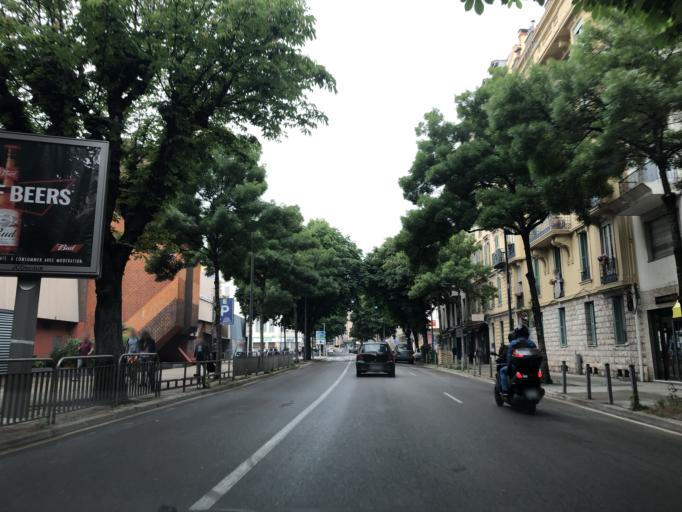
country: FR
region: Provence-Alpes-Cote d'Azur
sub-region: Departement des Alpes-Maritimes
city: Villefranche-sur-Mer
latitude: 43.7069
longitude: 7.2872
